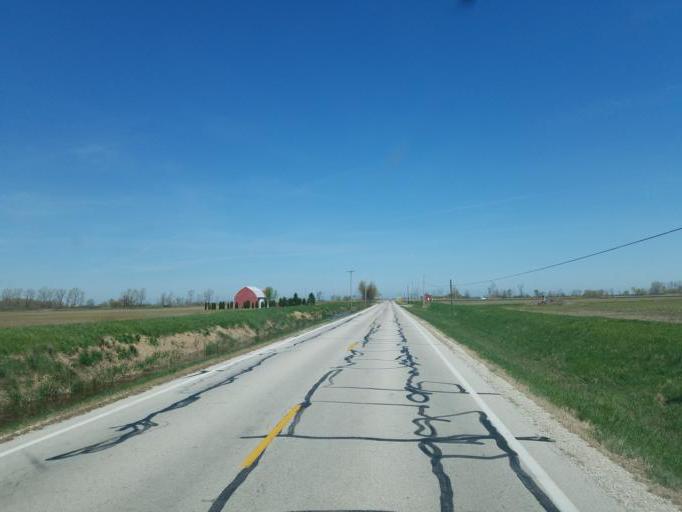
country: US
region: Ohio
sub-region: Ottawa County
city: Oak Harbor
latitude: 41.5989
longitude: -83.1451
